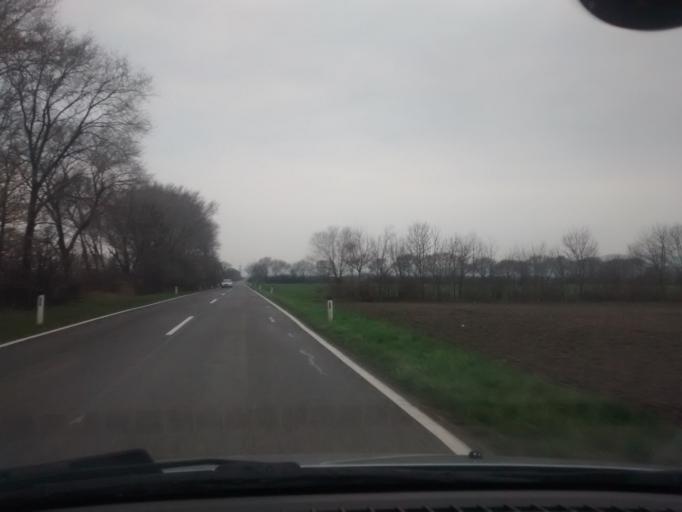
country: AT
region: Lower Austria
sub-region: Politischer Bezirk Modling
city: Munchendorf
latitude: 48.0021
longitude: 16.4034
